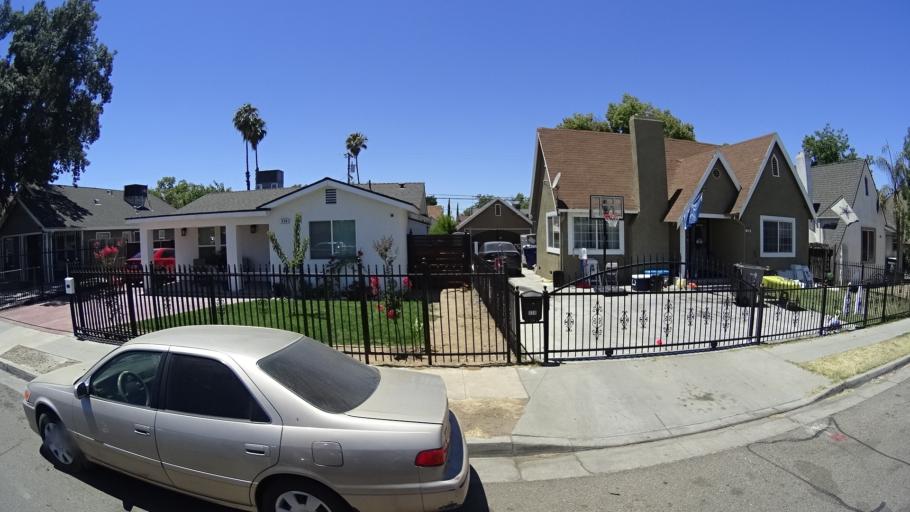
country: US
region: California
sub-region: Fresno County
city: Fresno
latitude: 36.7407
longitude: -119.7456
